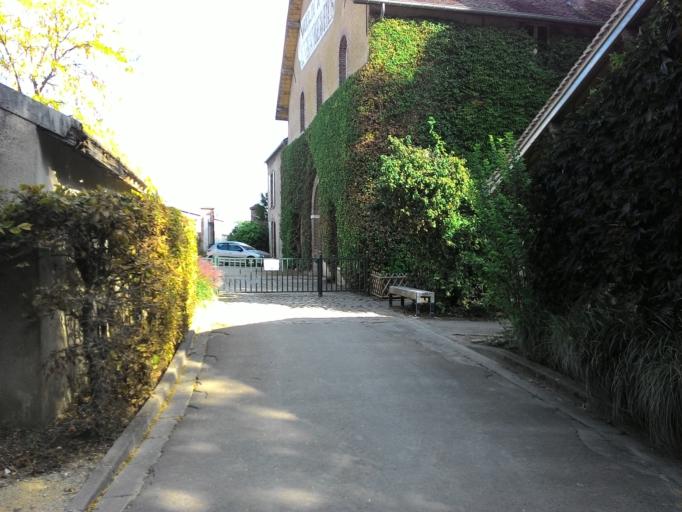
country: FR
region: Bourgogne
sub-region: Departement de l'Yonne
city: Sens
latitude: 48.1855
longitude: 3.2785
